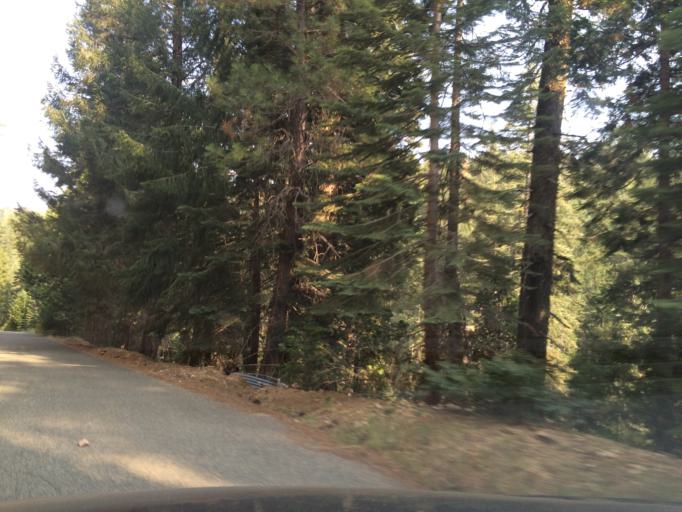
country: US
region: California
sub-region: Sierra County
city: Downieville
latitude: 39.3790
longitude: -120.6732
